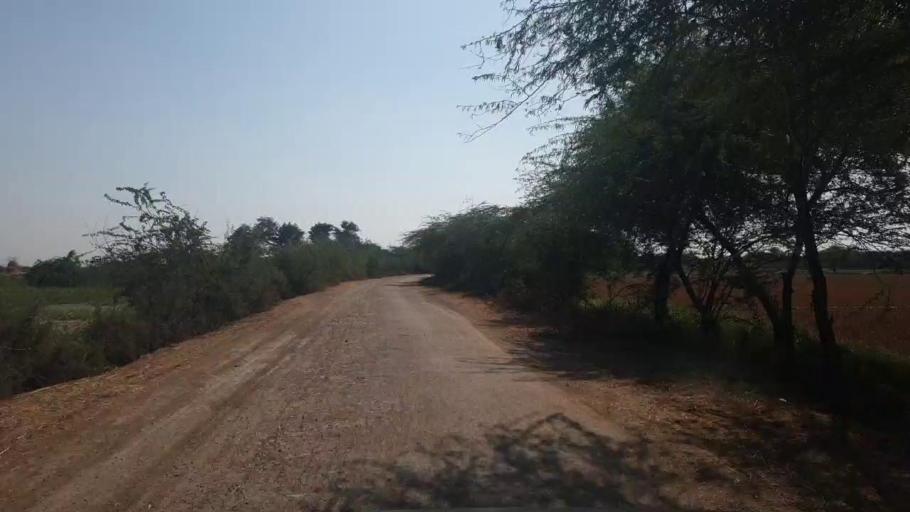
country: PK
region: Sindh
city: Badin
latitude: 24.6024
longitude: 68.8544
